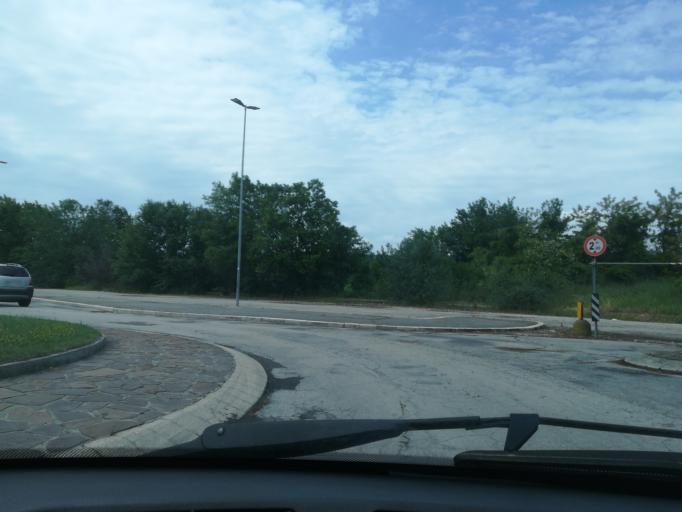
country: IT
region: The Marches
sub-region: Provincia di Macerata
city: Piediripa
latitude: 43.2815
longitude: 13.5029
